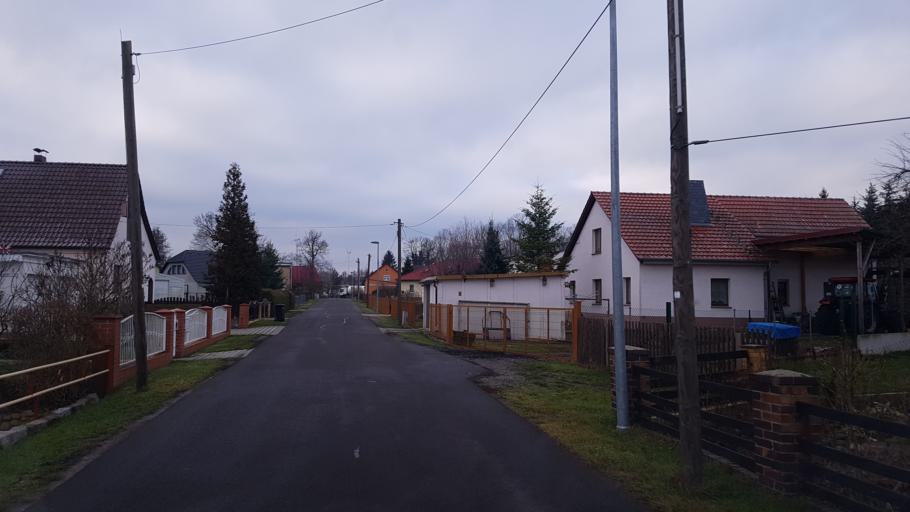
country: DE
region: Brandenburg
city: Schipkau
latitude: 51.5456
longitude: 13.8991
